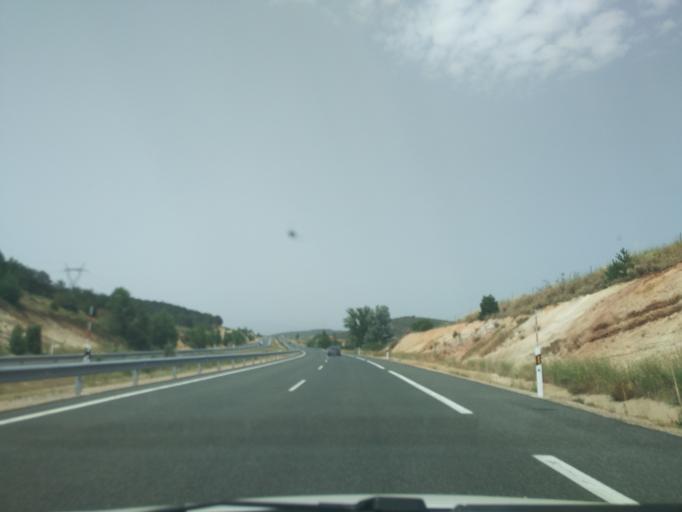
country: ES
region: Castille and Leon
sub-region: Provincia de Palencia
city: Aguilar de Campoo
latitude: 42.7402
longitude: -4.2895
